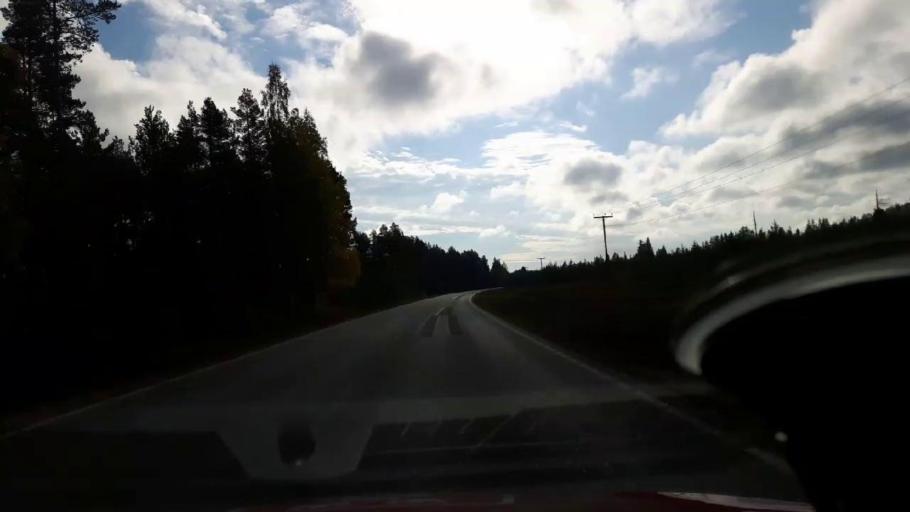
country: SE
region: Jaemtland
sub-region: Harjedalens Kommun
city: Sveg
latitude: 62.1122
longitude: 15.0566
